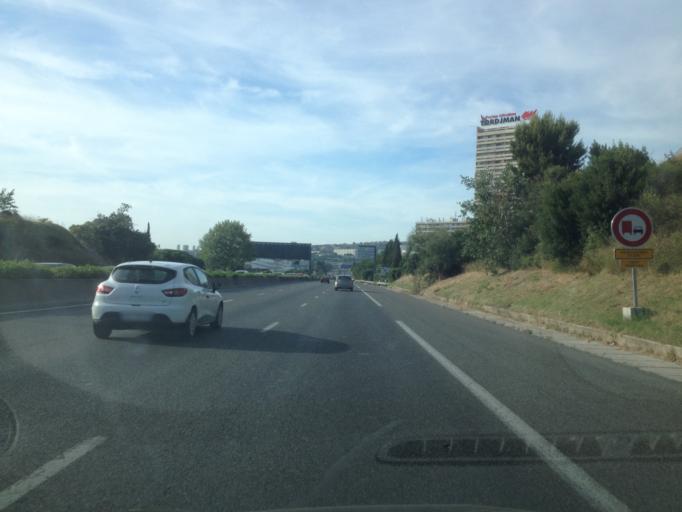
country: FR
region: Provence-Alpes-Cote d'Azur
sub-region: Departement des Bouches-du-Rhone
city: Marseille 14
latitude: 43.3286
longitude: 5.3781
